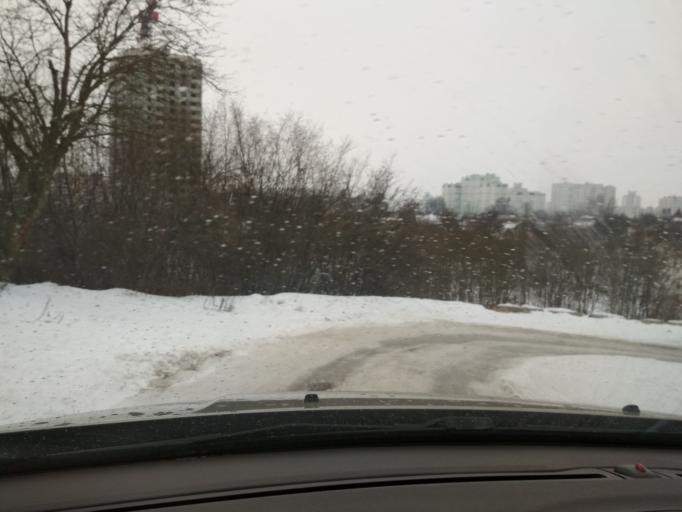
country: BY
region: Minsk
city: Novoye Medvezhino
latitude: 53.9046
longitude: 27.4285
